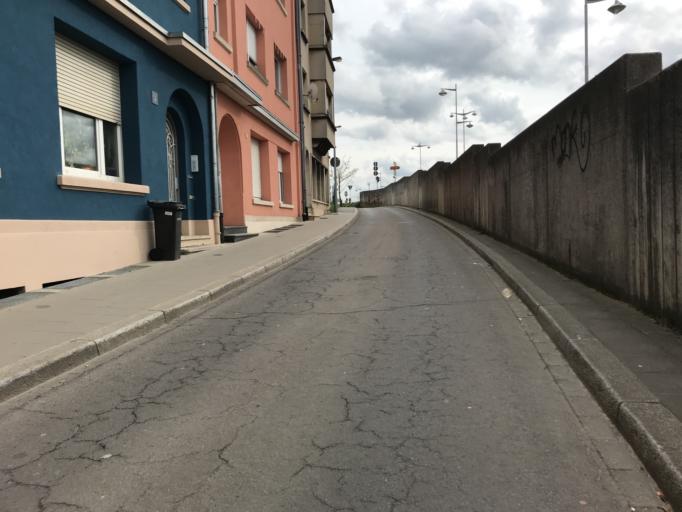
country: LU
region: Luxembourg
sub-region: Canton de Luxembourg
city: Luxembourg
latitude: 49.5963
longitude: 6.1335
